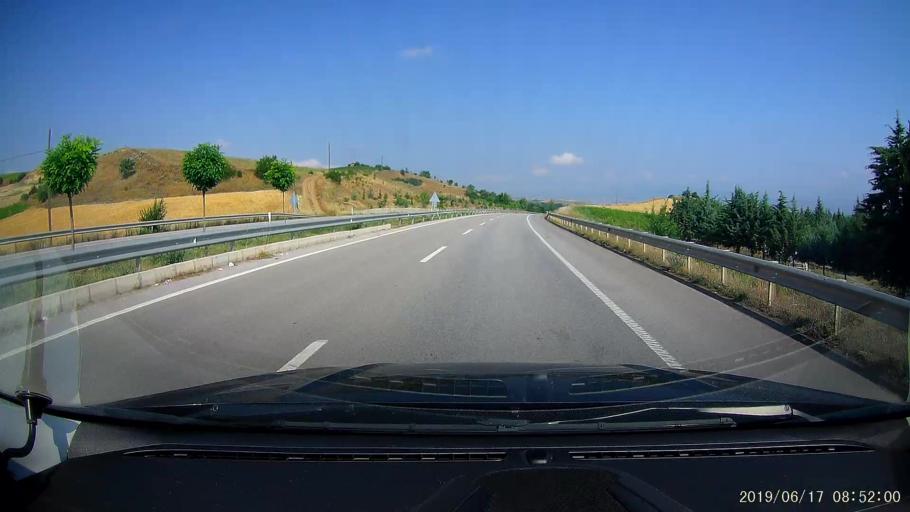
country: TR
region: Tokat
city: Erbaa
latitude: 40.6922
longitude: 36.5043
